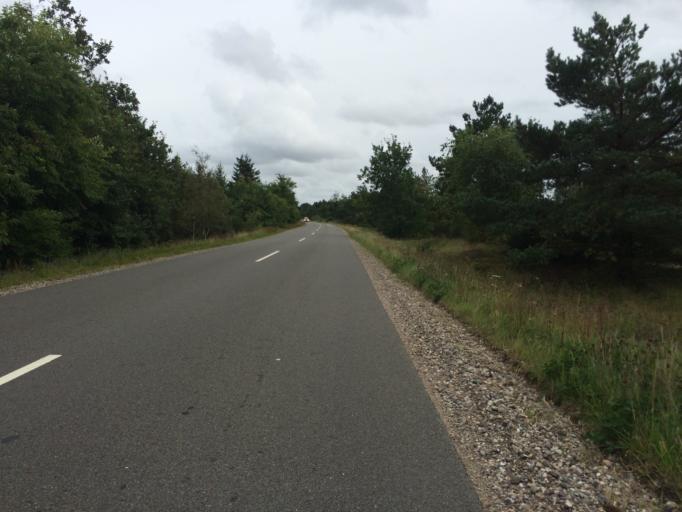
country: DK
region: Central Jutland
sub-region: Holstebro Kommune
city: Ulfborg
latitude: 56.2193
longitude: 8.3874
